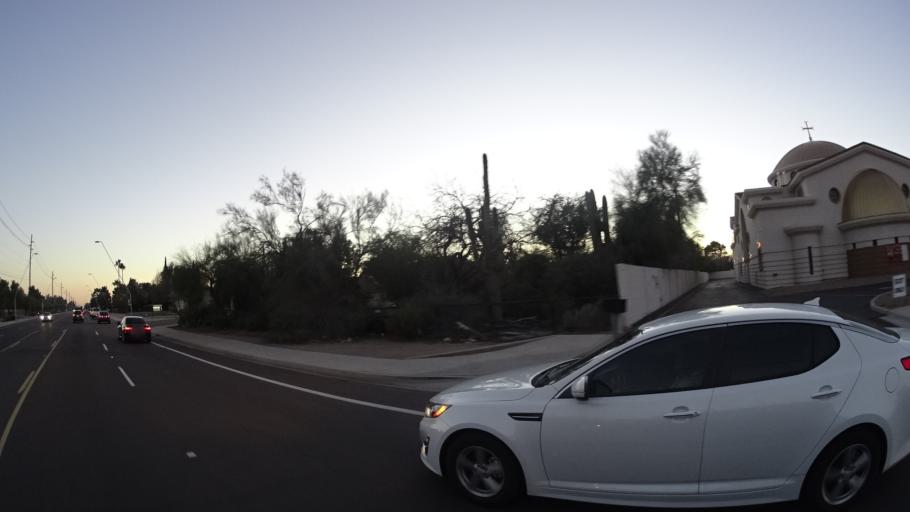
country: US
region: Arizona
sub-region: Maricopa County
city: San Carlos
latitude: 33.3465
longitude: -111.8765
